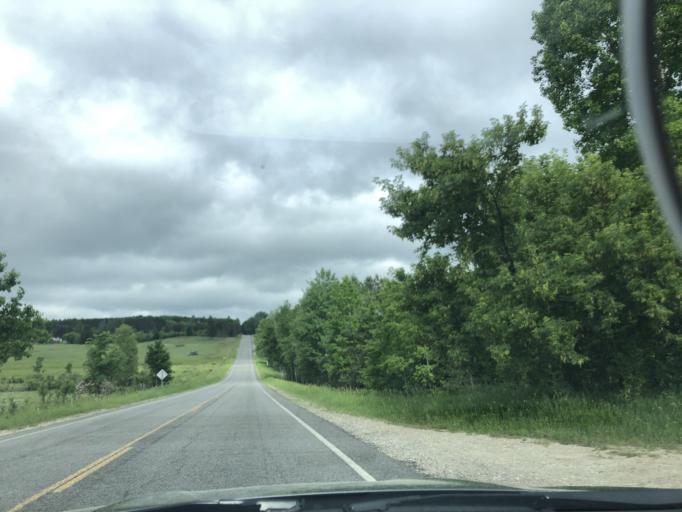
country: US
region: Michigan
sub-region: Missaukee County
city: Lake City
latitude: 44.4537
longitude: -85.2072
